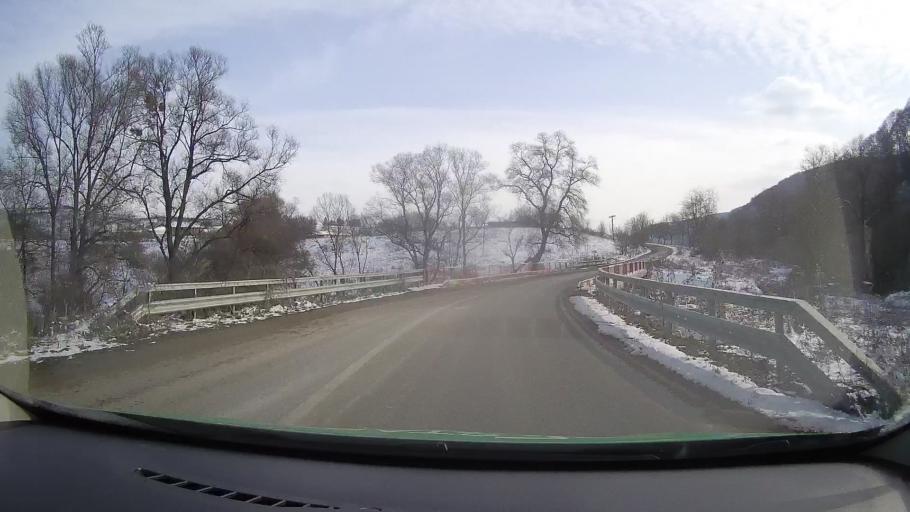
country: RO
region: Mures
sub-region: Comuna Apold
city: Saes
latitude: 46.1647
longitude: 24.7585
